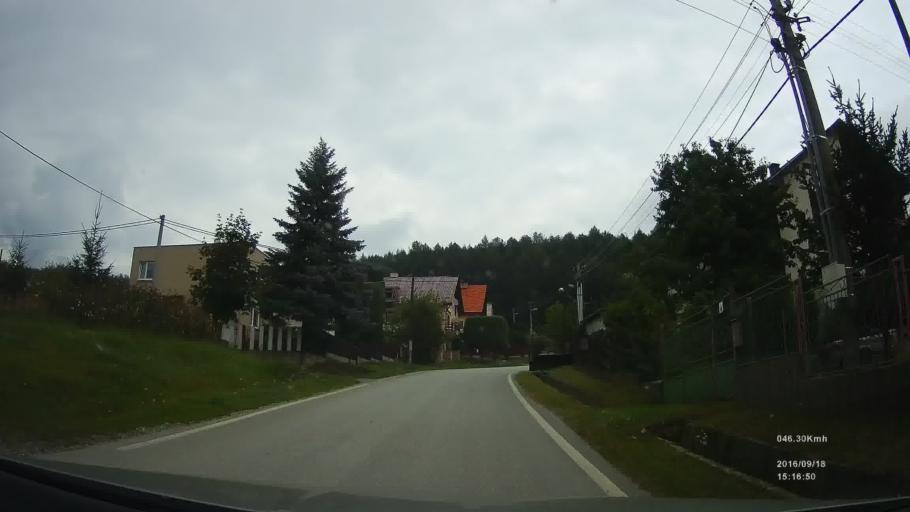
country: SK
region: Presovsky
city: Lubica
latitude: 49.0218
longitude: 20.4856
